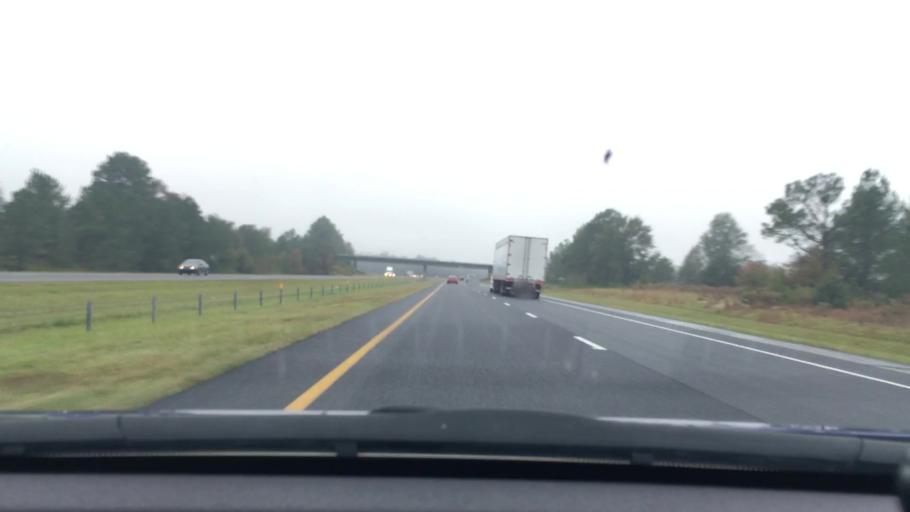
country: US
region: South Carolina
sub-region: Florence County
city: Timmonsville
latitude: 34.2001
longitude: -80.0653
